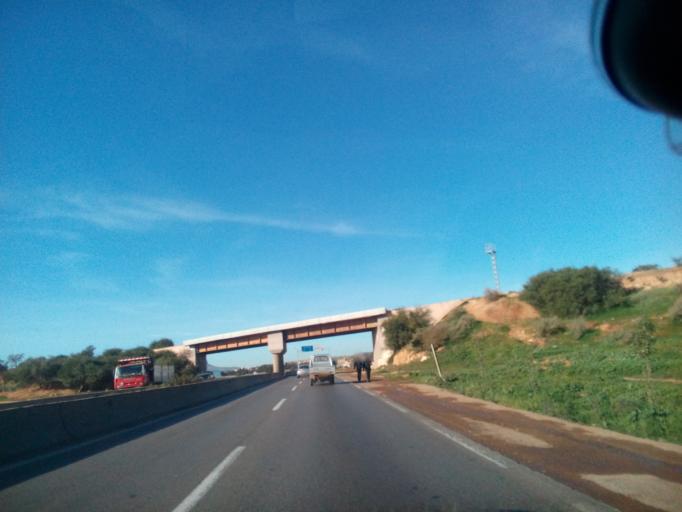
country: DZ
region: Oran
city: Ain el Bya
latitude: 35.7989
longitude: -0.3616
